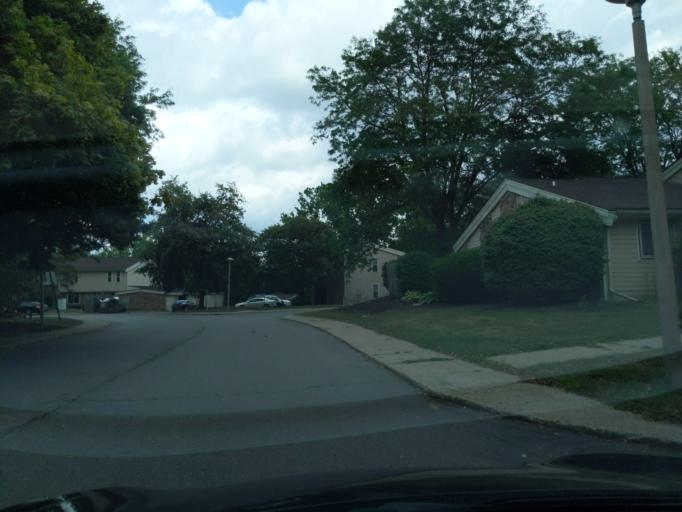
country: US
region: Michigan
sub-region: Ingham County
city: Holt
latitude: 42.6564
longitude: -84.5418
